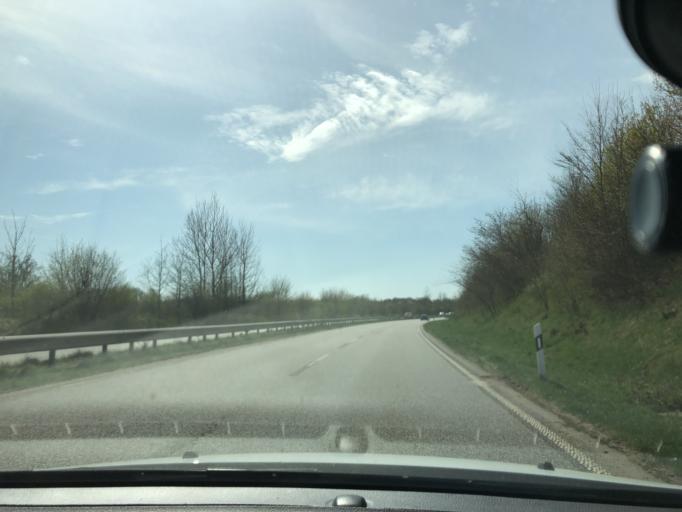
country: DE
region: Schleswig-Holstein
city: Flensburg
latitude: 54.7635
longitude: 9.4566
